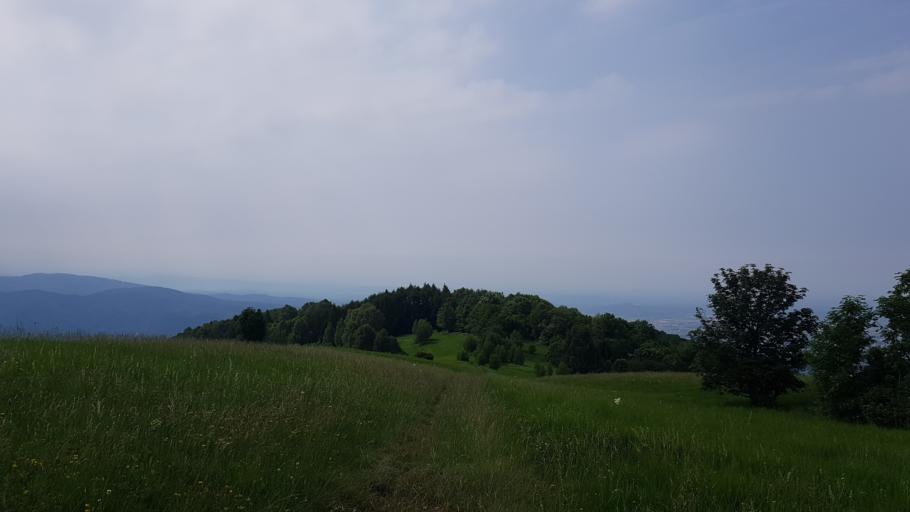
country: IT
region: Friuli Venezia Giulia
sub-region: Provincia di Udine
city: Pulfero
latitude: 46.1709
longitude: 13.4457
